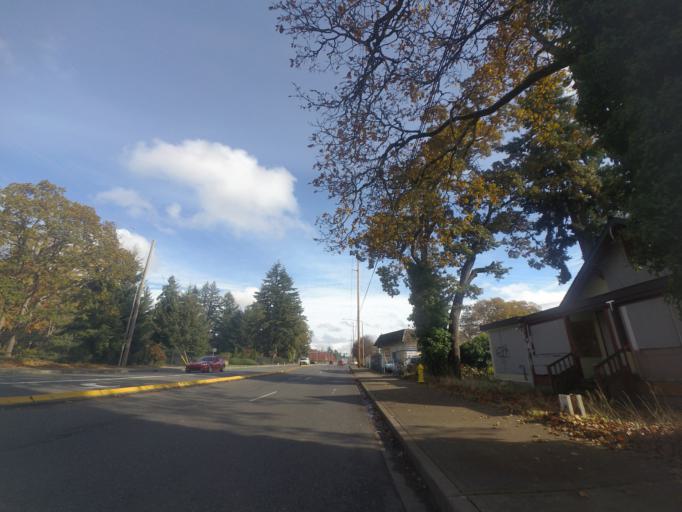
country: US
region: Washington
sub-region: Pierce County
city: Lakewood
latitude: 47.1764
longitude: -122.5101
